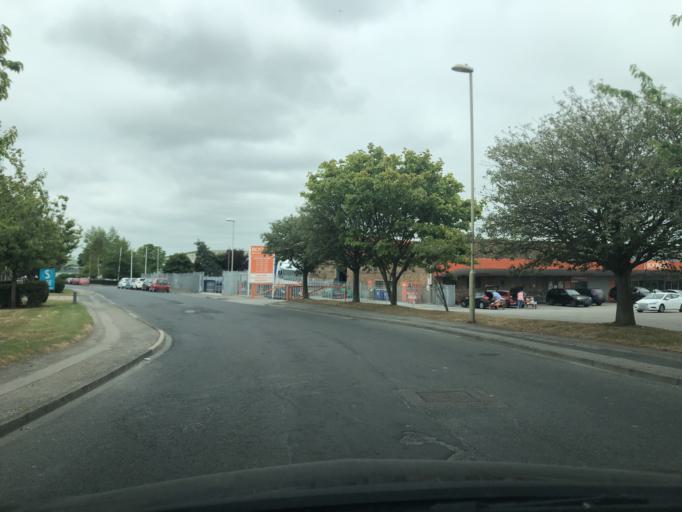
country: GB
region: England
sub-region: North Yorkshire
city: Scarborough
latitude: 54.2391
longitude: -0.4079
